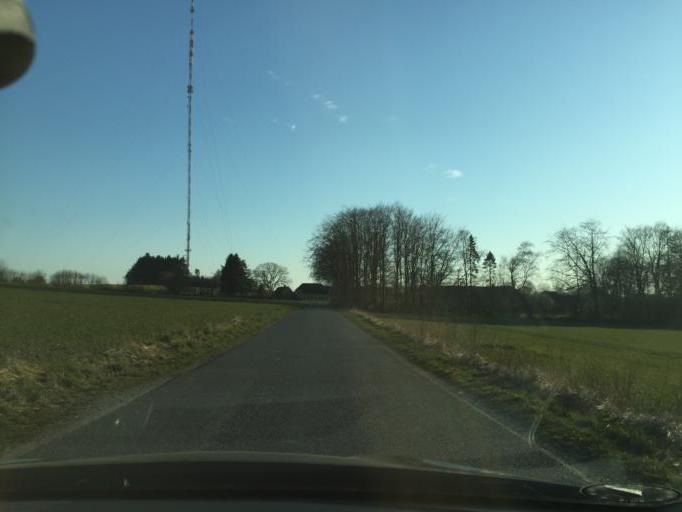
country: DK
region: South Denmark
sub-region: Faaborg-Midtfyn Kommune
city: Arslev
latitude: 55.2868
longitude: 10.4760
